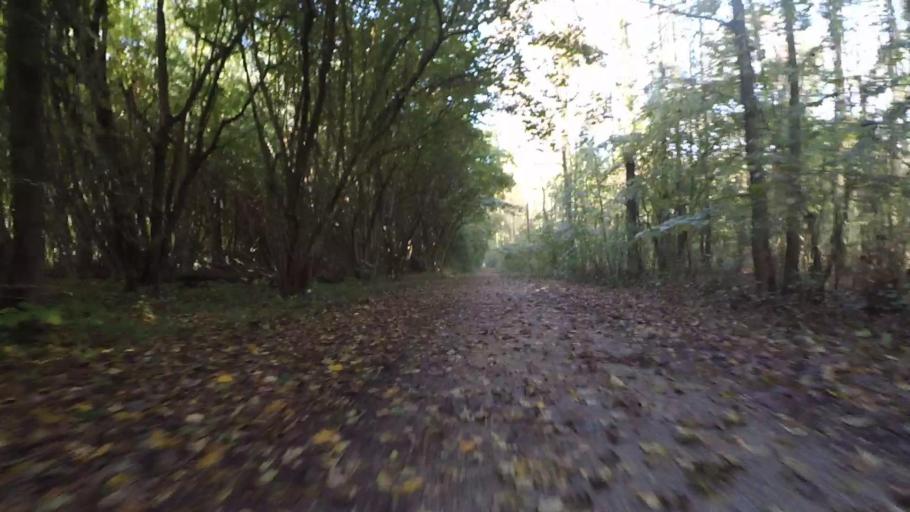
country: NL
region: Flevoland
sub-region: Gemeente Zeewolde
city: Zeewolde
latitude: 52.3008
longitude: 5.5324
